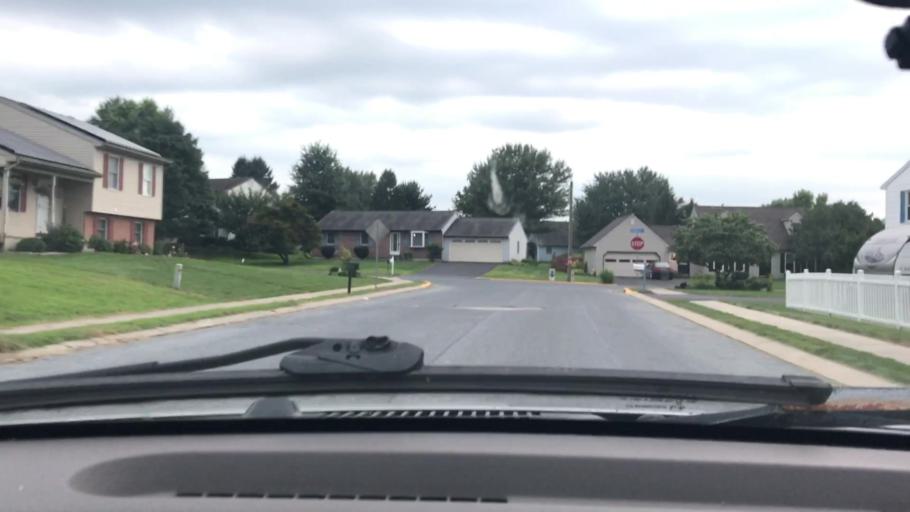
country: US
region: Pennsylvania
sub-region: Lancaster County
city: Elizabethtown
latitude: 40.1627
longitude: -76.5842
